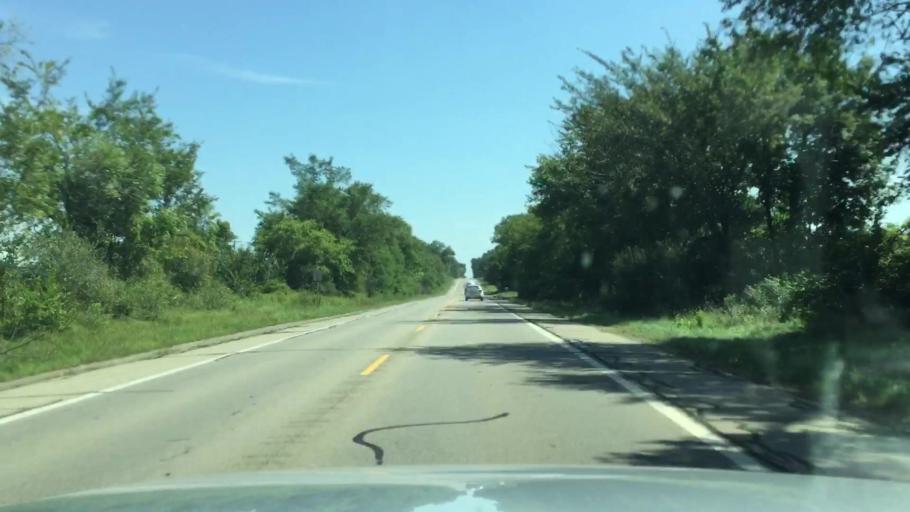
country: US
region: Michigan
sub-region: Washtenaw County
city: Manchester
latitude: 42.0727
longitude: -84.0571
